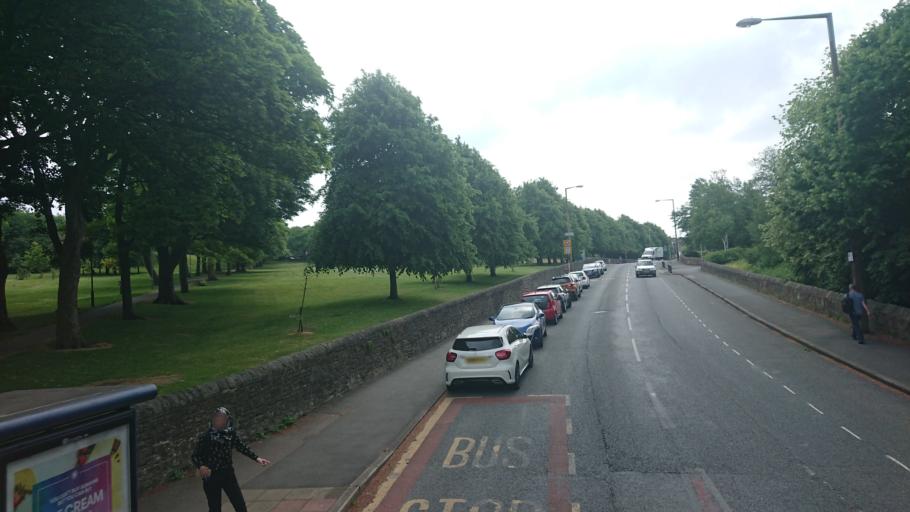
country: GB
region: England
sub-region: Lancashire
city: Lancaster
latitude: 54.0420
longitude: -2.7925
